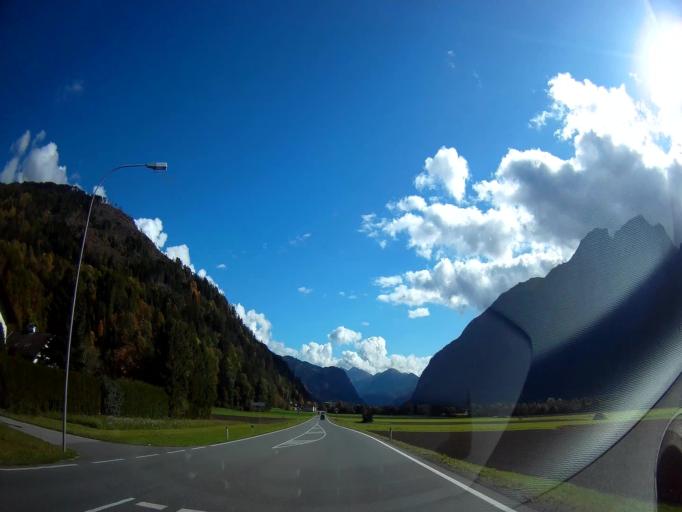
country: AT
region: Tyrol
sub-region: Politischer Bezirk Lienz
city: Lavant
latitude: 46.8120
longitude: 12.8471
